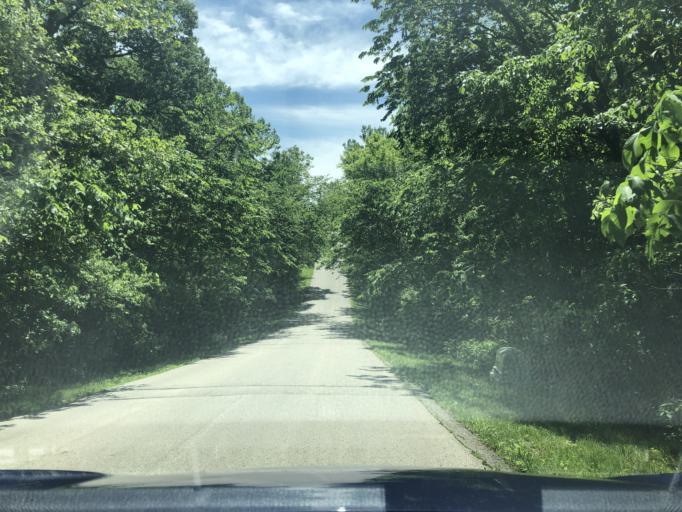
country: US
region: Missouri
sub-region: Platte County
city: Weston
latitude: 39.3934
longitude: -94.8699
